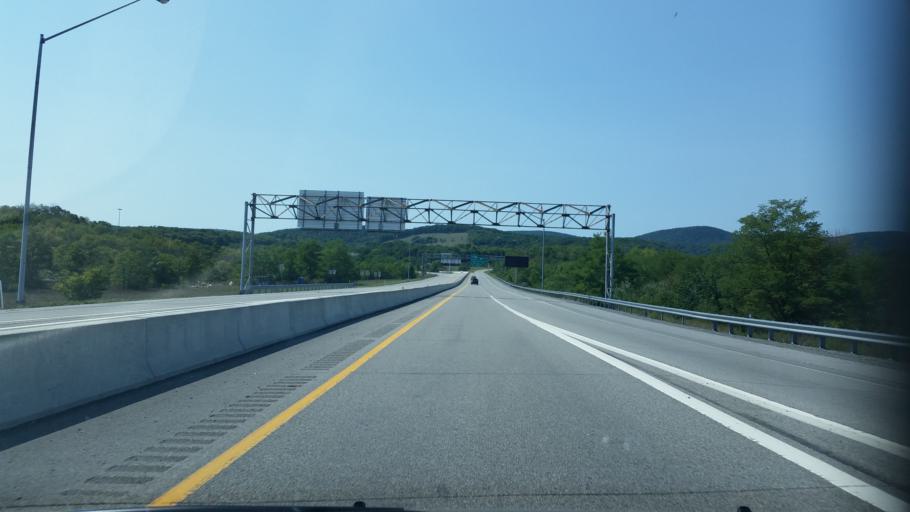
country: US
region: Pennsylvania
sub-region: Blair County
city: Duncansville
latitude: 40.4450
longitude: -78.4355
